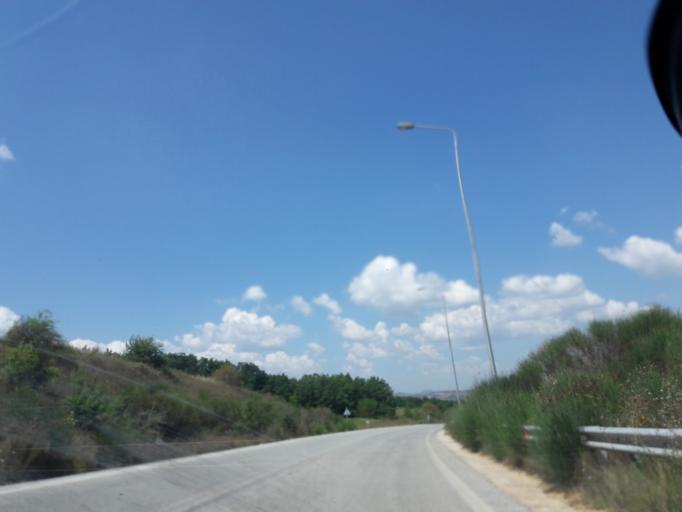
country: GR
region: Central Macedonia
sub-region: Nomos Chalkidikis
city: Polygyros
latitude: 40.4557
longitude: 23.4066
